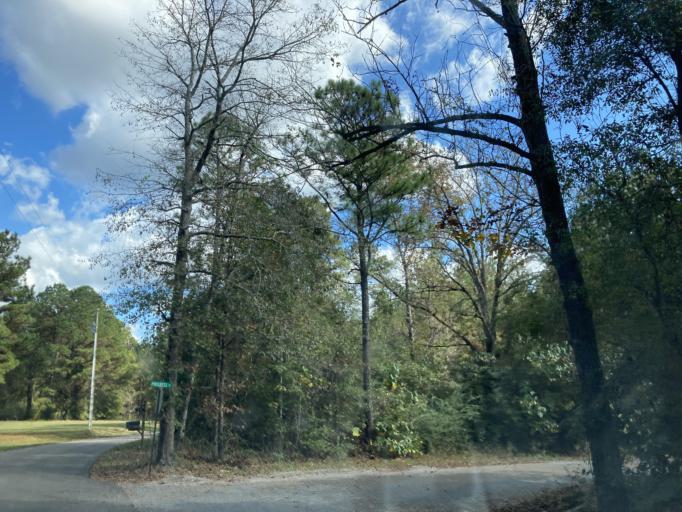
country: US
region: Mississippi
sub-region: Lamar County
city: Sumrall
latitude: 31.3740
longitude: -89.5428
